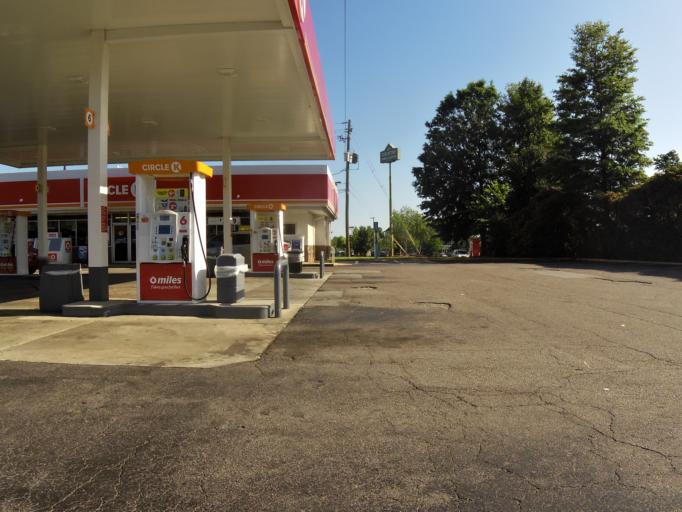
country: US
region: Georgia
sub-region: Columbia County
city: Martinez
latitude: 33.5114
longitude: -82.0376
